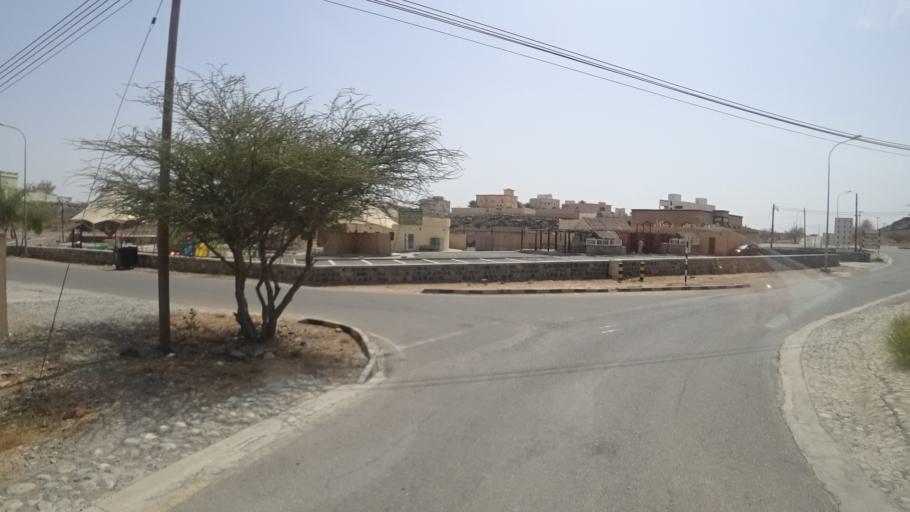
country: OM
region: Muhafazat ad Dakhiliyah
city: Bahla'
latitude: 23.1383
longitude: 57.3068
